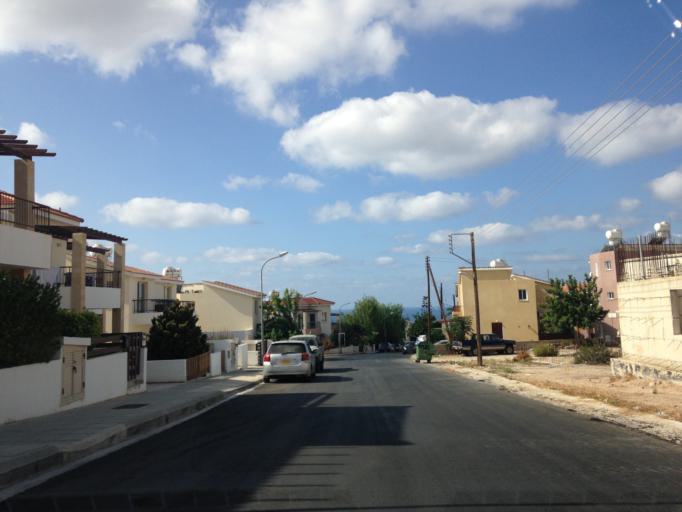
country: CY
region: Pafos
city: Pegeia
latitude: 34.8754
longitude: 32.3728
